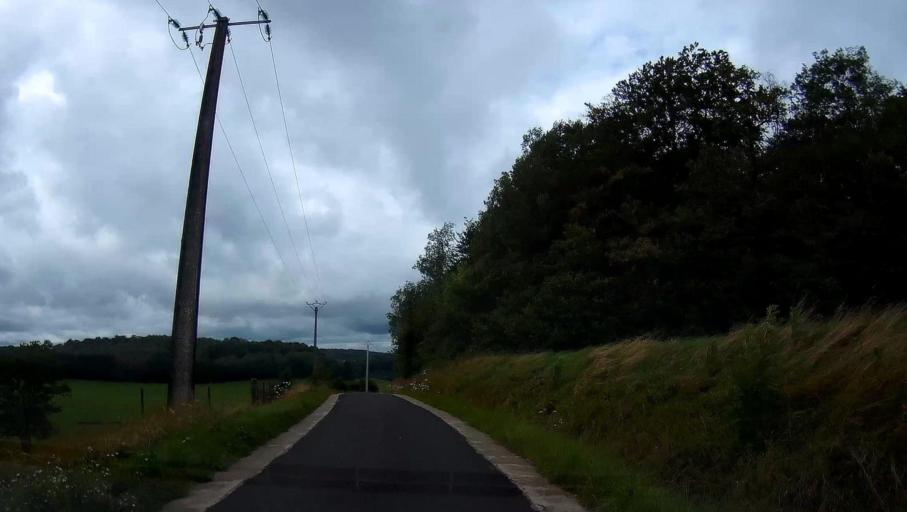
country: FR
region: Champagne-Ardenne
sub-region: Departement des Ardennes
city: Rimogne
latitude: 49.7657
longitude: 4.4984
